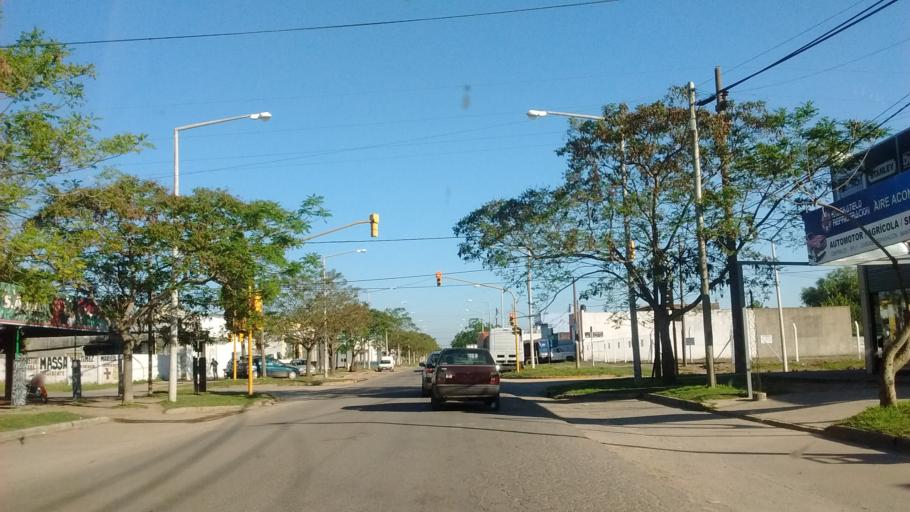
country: AR
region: Santa Fe
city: Venado Tuerto
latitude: -33.7320
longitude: -61.9793
